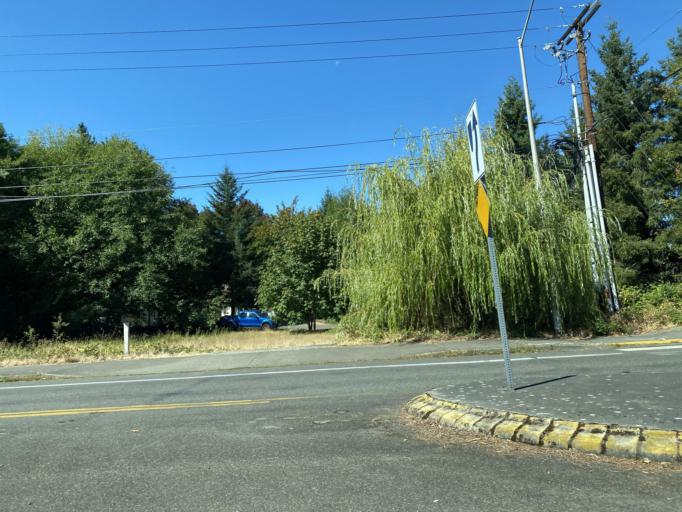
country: US
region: Washington
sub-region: Thurston County
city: Olympia
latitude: 47.0346
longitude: -122.8868
